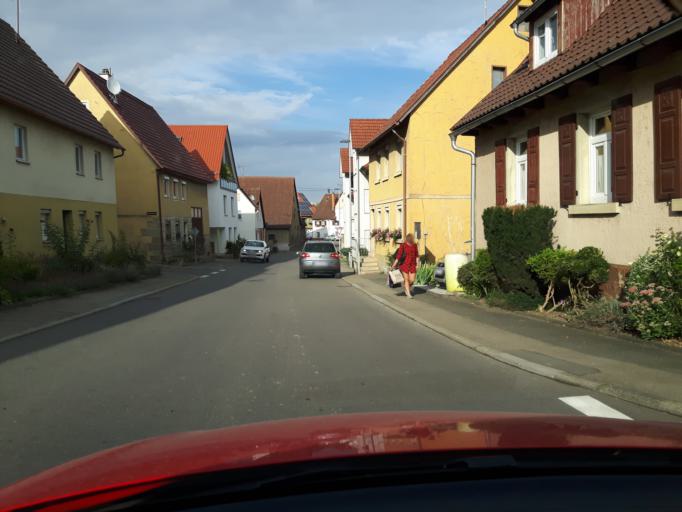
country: DE
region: Baden-Wuerttemberg
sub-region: Regierungsbezirk Stuttgart
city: Brackenheim
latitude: 49.0770
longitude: 9.1038
